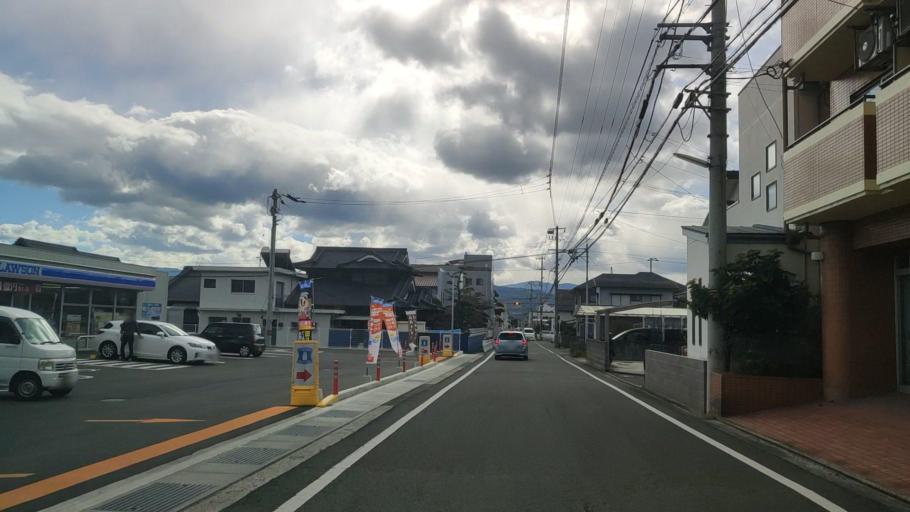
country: JP
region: Ehime
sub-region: Shikoku-chuo Shi
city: Matsuyama
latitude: 33.8140
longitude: 132.7525
